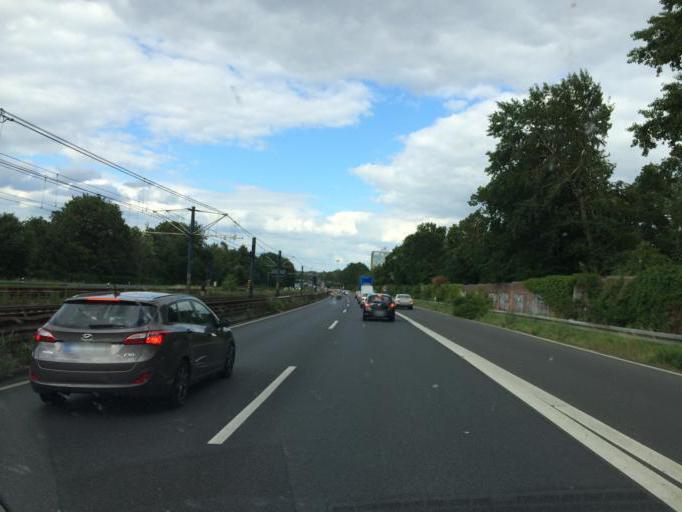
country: DE
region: North Rhine-Westphalia
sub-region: Regierungsbezirk Dusseldorf
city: Muelheim (Ruhr)
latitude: 51.4356
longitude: 6.9414
